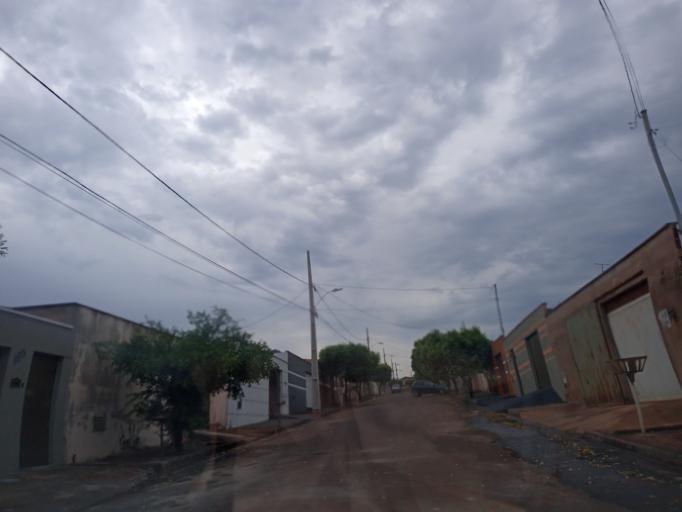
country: BR
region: Minas Gerais
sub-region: Ituiutaba
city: Ituiutaba
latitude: -18.9738
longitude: -49.4881
